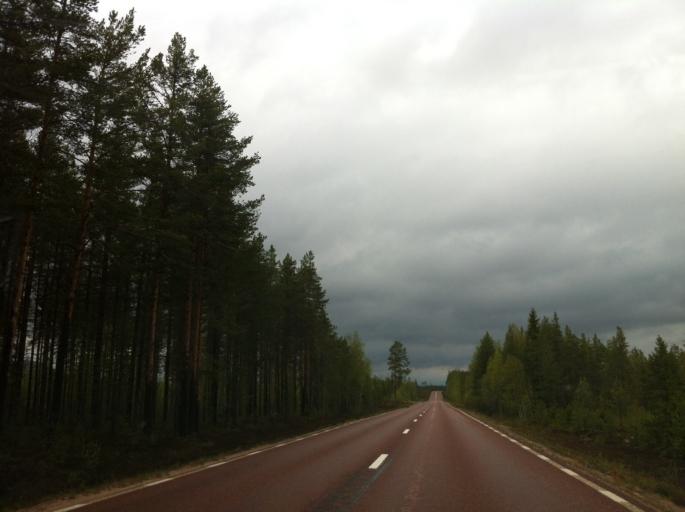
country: SE
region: Jaemtland
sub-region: Harjedalens Kommun
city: Sveg
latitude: 61.8983
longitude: 14.6232
